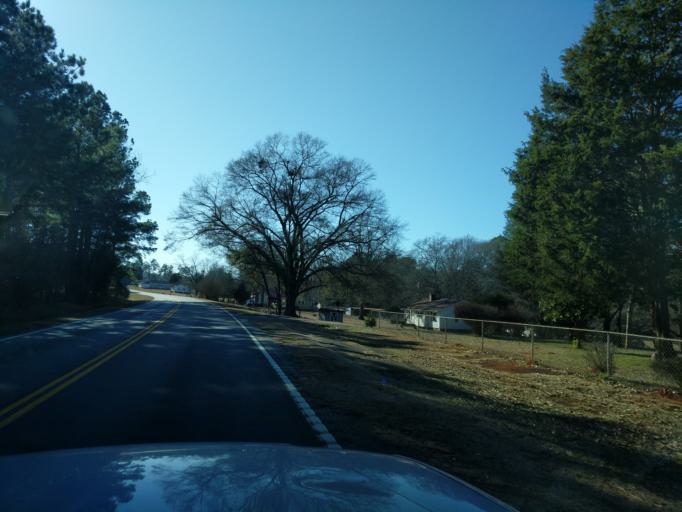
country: US
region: South Carolina
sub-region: Anderson County
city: Homeland Park
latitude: 34.4406
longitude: -82.7331
